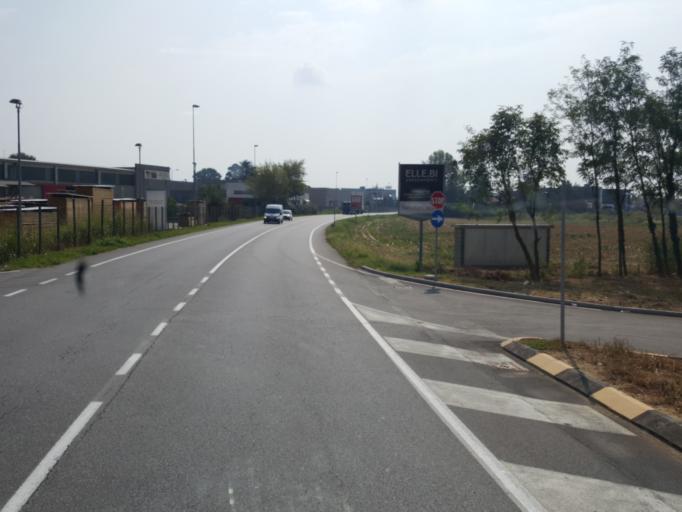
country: IT
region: Lombardy
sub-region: Provincia di Bergamo
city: Telgate
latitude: 45.6364
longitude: 9.8564
